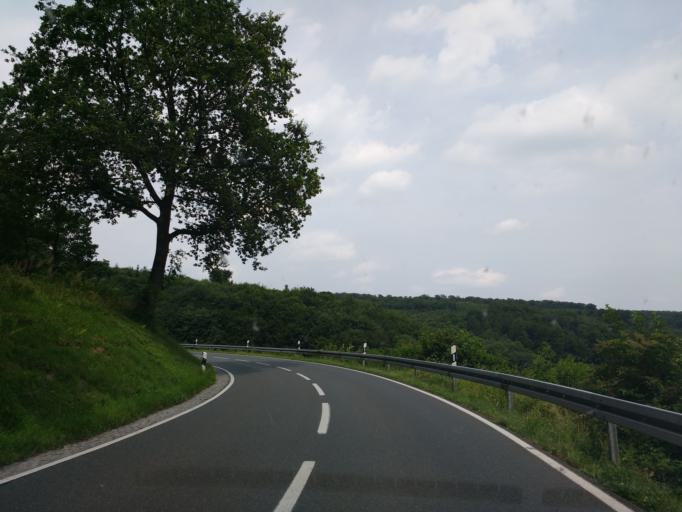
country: DE
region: Lower Saxony
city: Bad Pyrmont
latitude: 51.9964
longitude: 9.2108
